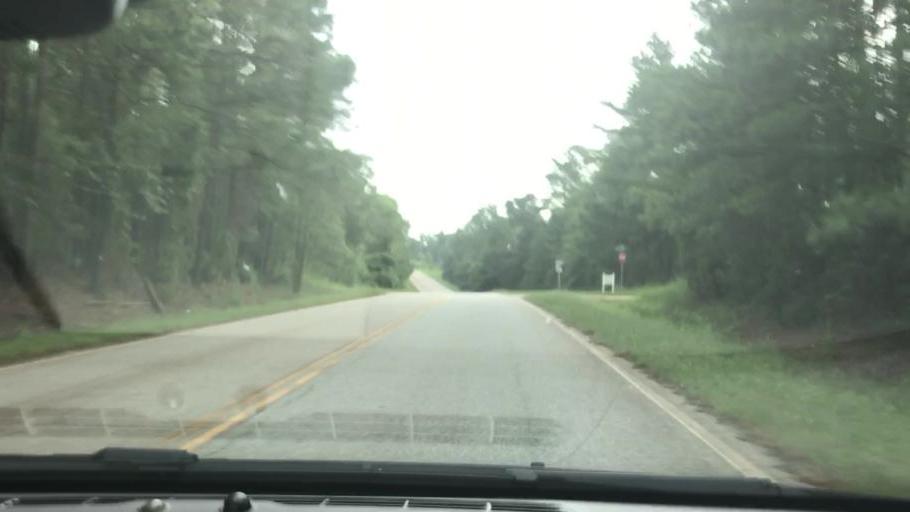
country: US
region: Georgia
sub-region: Quitman County
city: Georgetown
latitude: 31.9246
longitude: -85.0189
